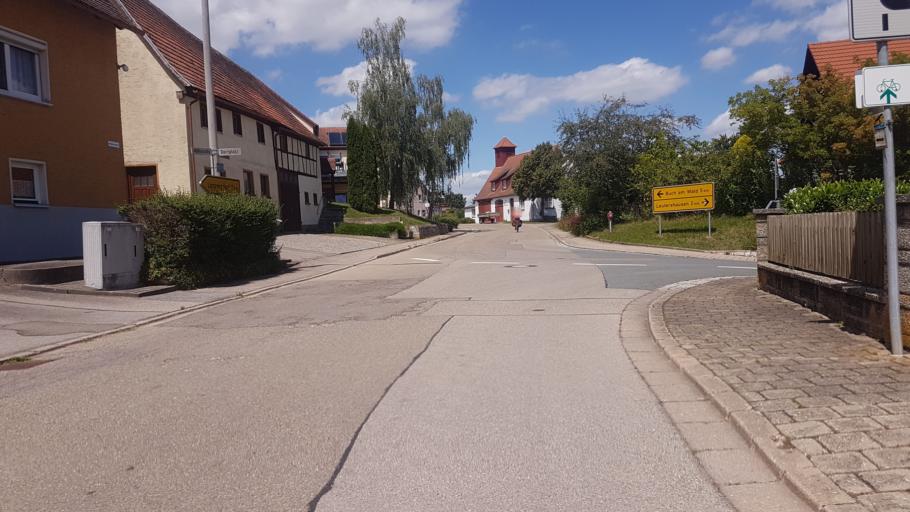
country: DE
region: Bavaria
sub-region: Regierungsbezirk Mittelfranken
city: Leutershausen
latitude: 49.3120
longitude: 10.3887
